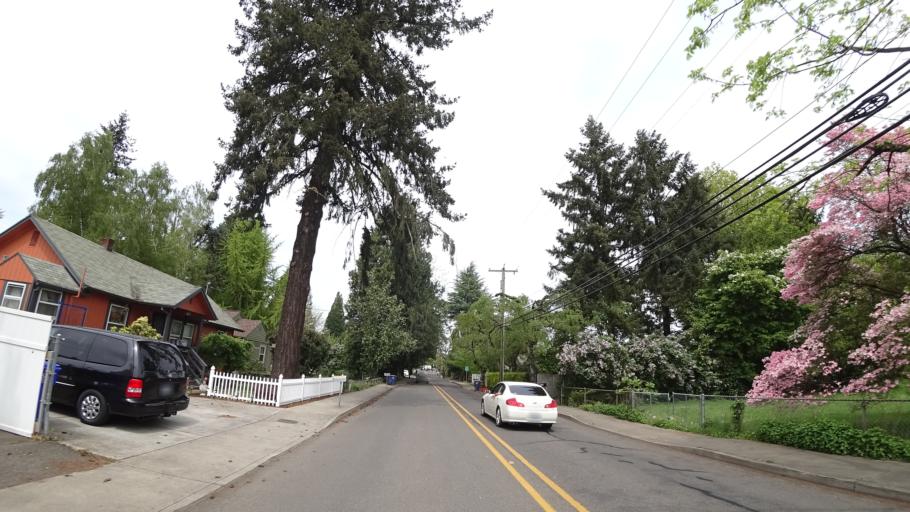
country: US
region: Oregon
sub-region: Clackamas County
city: Milwaukie
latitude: 45.4540
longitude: -122.6202
